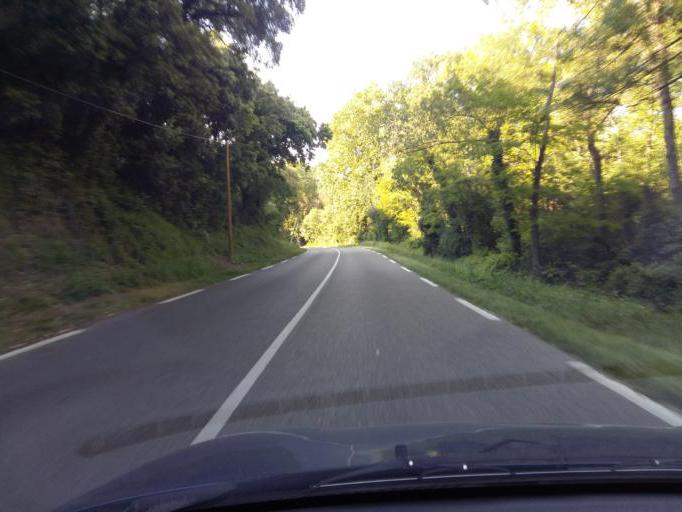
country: FR
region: Languedoc-Roussillon
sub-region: Departement du Gard
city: Sauveterre
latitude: 44.0028
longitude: 4.8120
